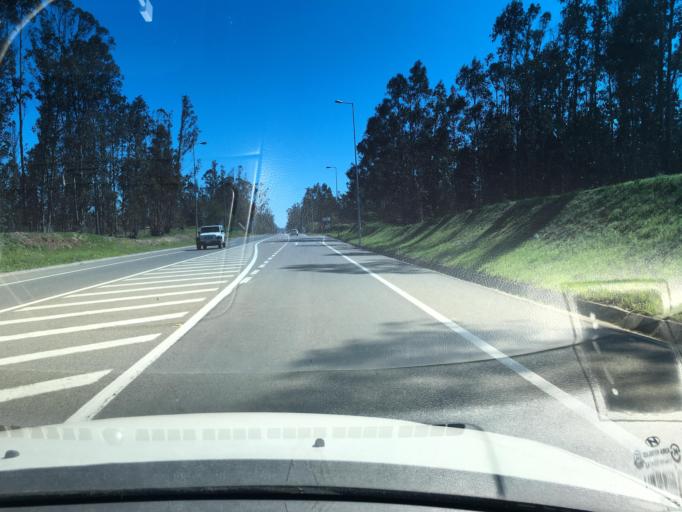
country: CL
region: Valparaiso
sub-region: San Antonio Province
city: El Tabo
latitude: -33.3999
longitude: -71.5873
